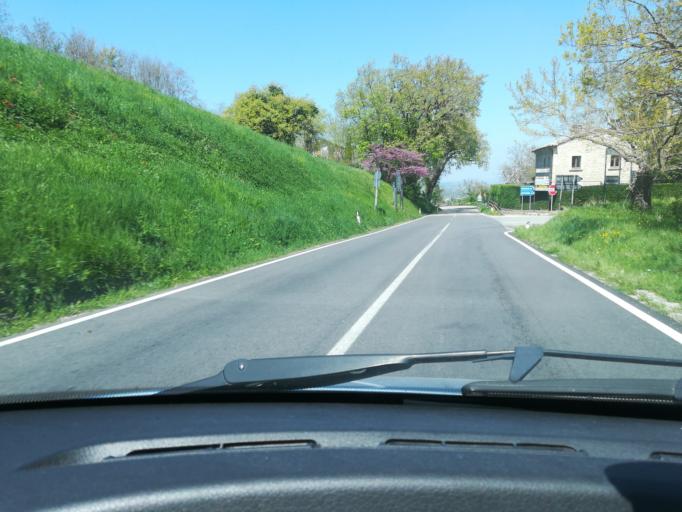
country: IT
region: The Marches
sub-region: Provincia di Macerata
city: Cingoli
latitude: 43.3781
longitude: 13.2163
